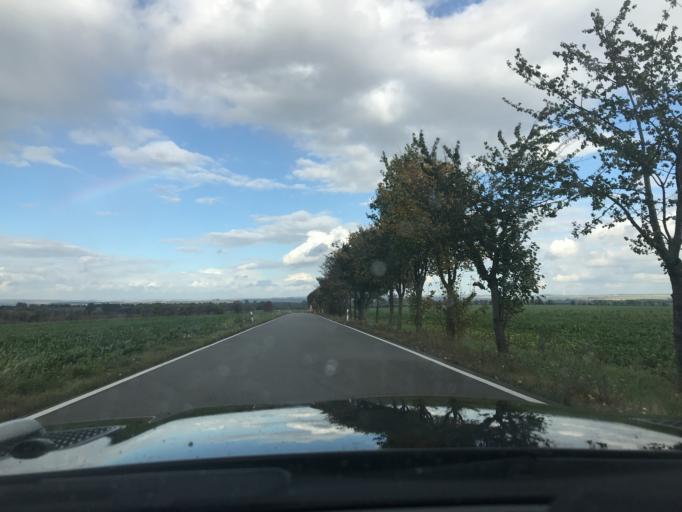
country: DE
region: Thuringia
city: Heroldishausen
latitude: 51.1278
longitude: 10.5149
